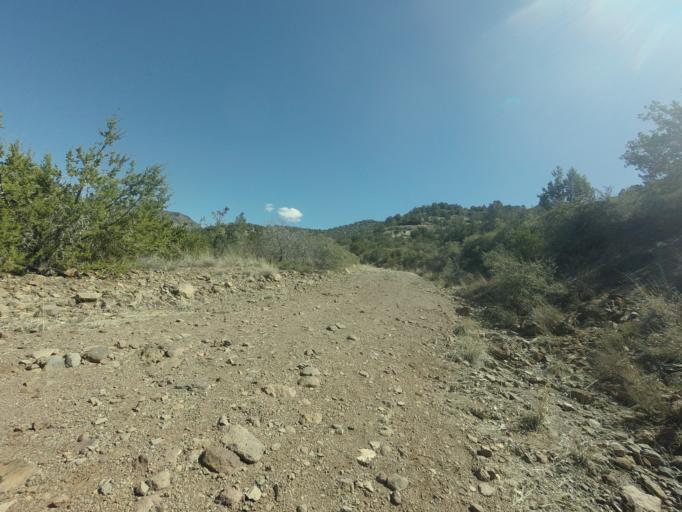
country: US
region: Arizona
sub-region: Gila County
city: Pine
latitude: 34.4061
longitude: -111.6085
